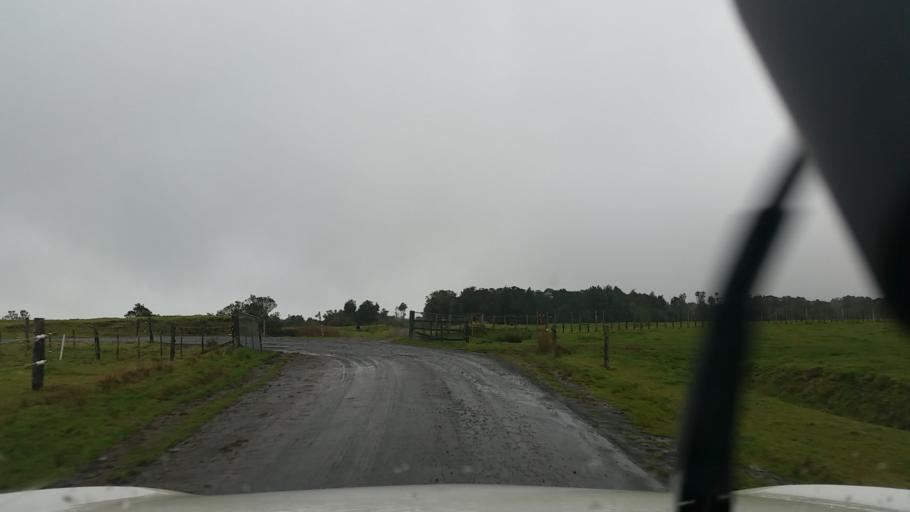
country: NZ
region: Taranaki
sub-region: South Taranaki District
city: Eltham
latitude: -39.2802
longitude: 174.1783
